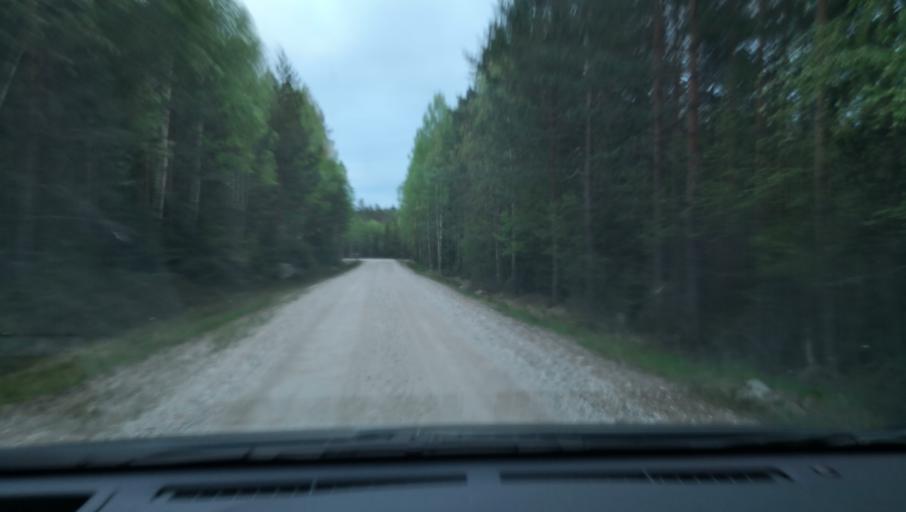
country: SE
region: Vaestmanland
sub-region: Skinnskattebergs Kommun
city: Skinnskatteberg
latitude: 59.7596
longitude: 15.4603
